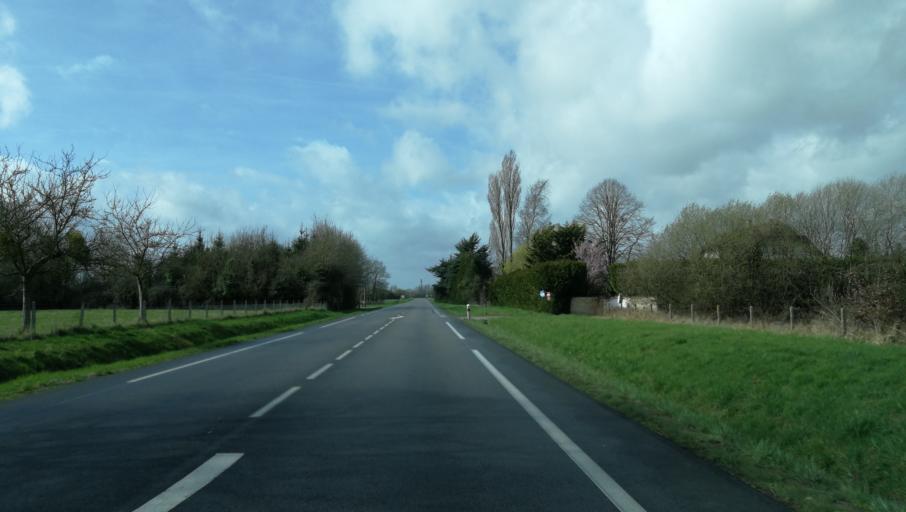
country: FR
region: Haute-Normandie
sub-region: Departement de l'Eure
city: Epaignes
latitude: 49.2825
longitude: 0.4210
